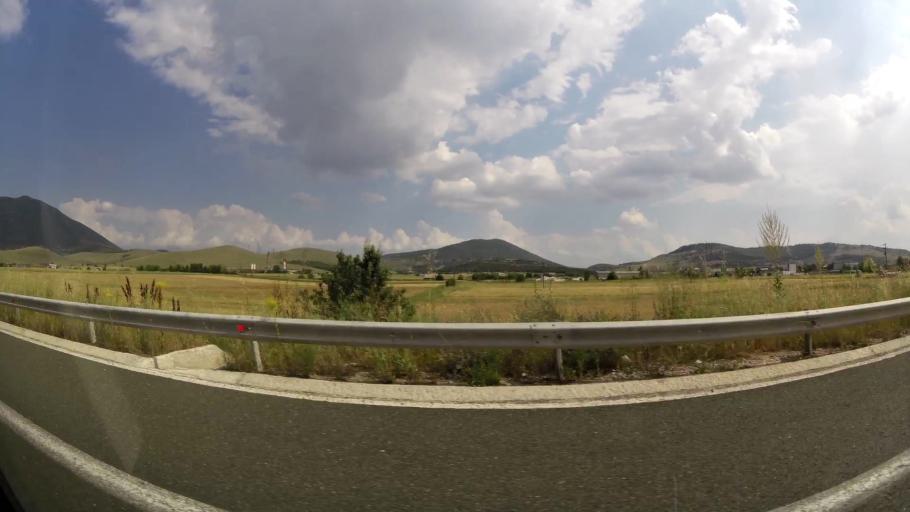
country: GR
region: West Macedonia
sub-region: Nomos Kozanis
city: Koila
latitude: 40.3612
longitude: 21.8508
